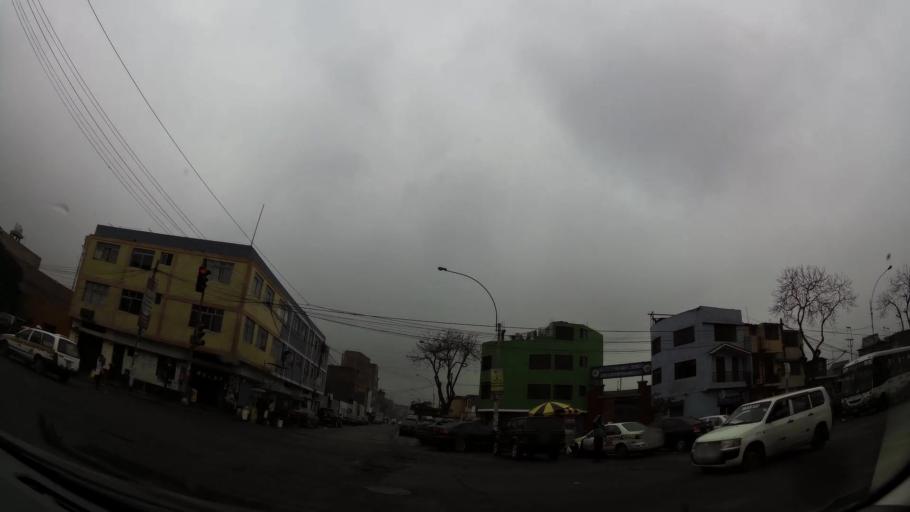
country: PE
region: Lima
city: Lima
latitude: -12.0628
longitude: -77.0263
